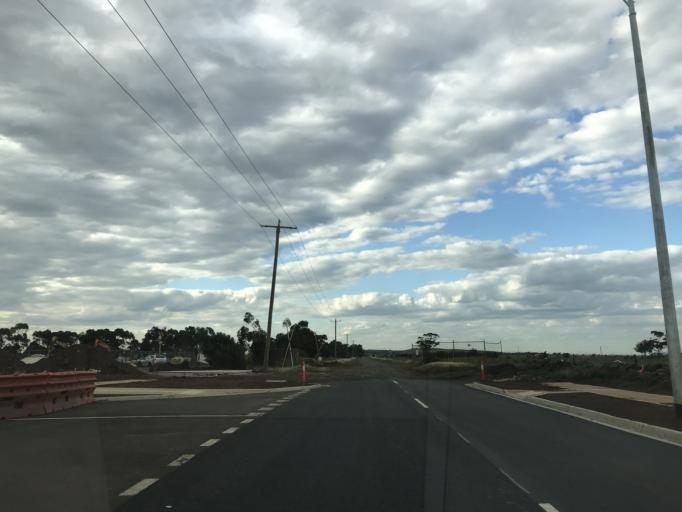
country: AU
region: Victoria
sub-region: Wyndham
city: Truganina
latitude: -37.8133
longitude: 144.7226
